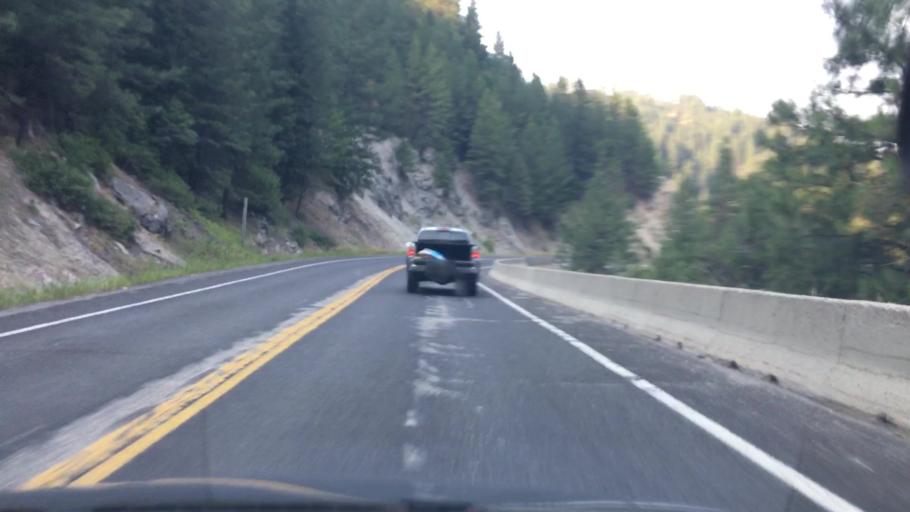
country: US
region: Idaho
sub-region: Valley County
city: Cascade
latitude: 44.2463
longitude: -116.0956
